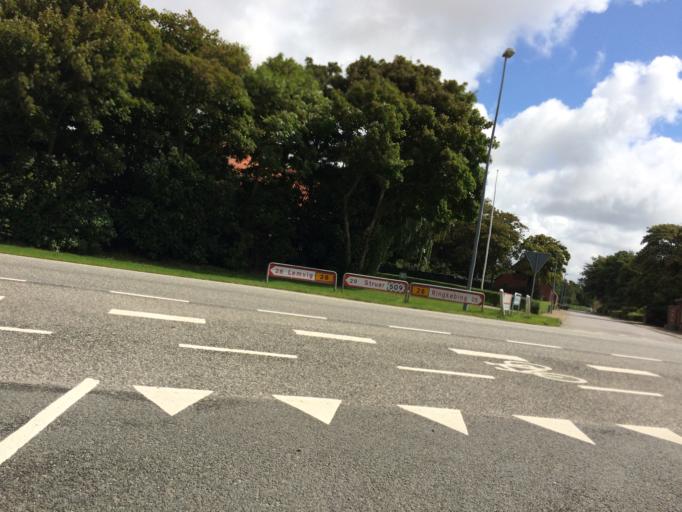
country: DK
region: Central Jutland
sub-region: Holstebro Kommune
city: Ulfborg
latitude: 56.3013
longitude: 8.3385
